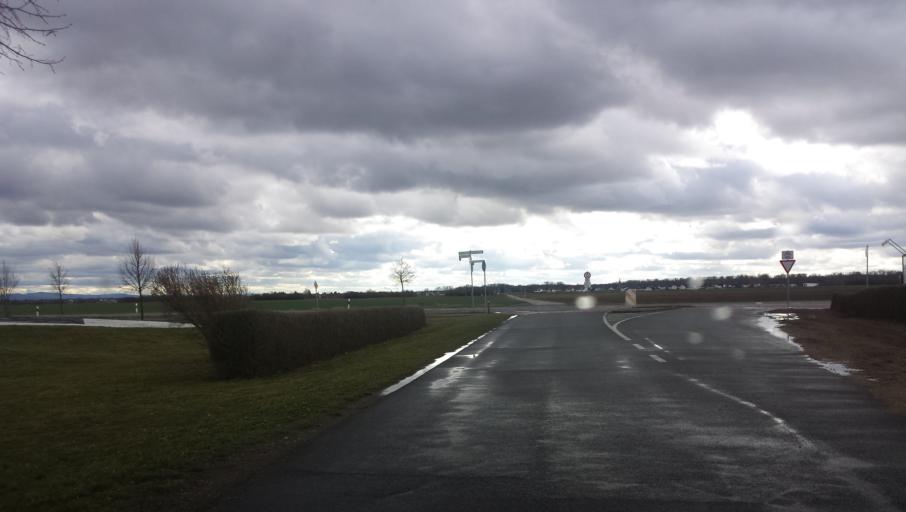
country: DE
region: Hesse
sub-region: Regierungsbezirk Darmstadt
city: Riedstadt
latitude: 49.8572
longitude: 8.4660
